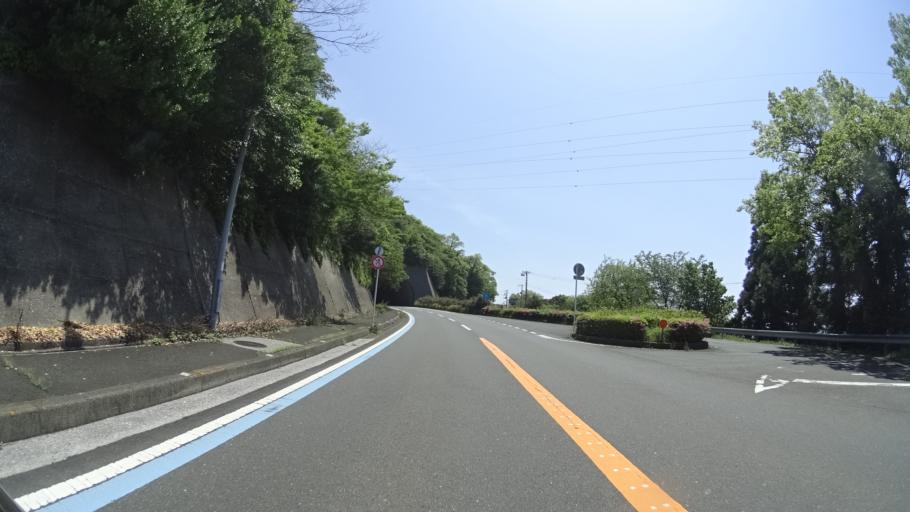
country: JP
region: Ehime
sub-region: Nishiuwa-gun
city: Ikata-cho
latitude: 33.4196
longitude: 132.1990
